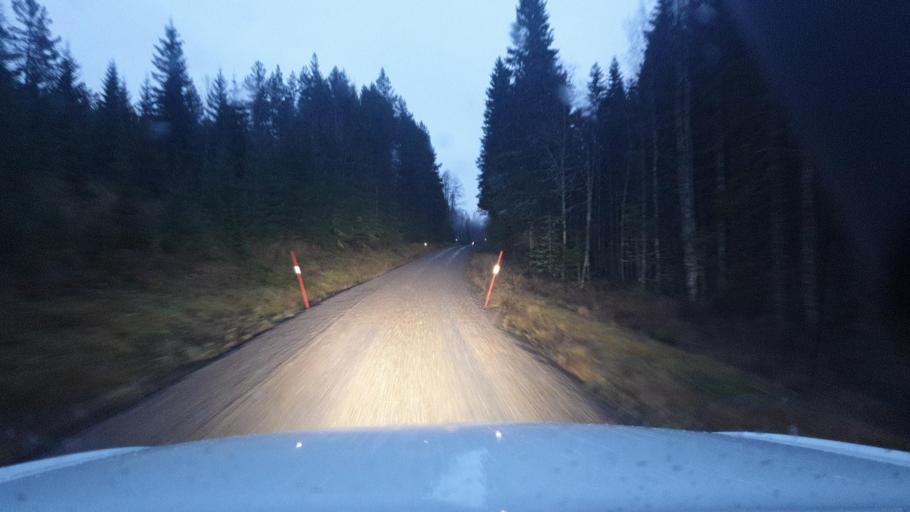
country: SE
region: Vaermland
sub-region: Eda Kommun
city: Charlottenberg
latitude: 60.0552
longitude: 12.6273
